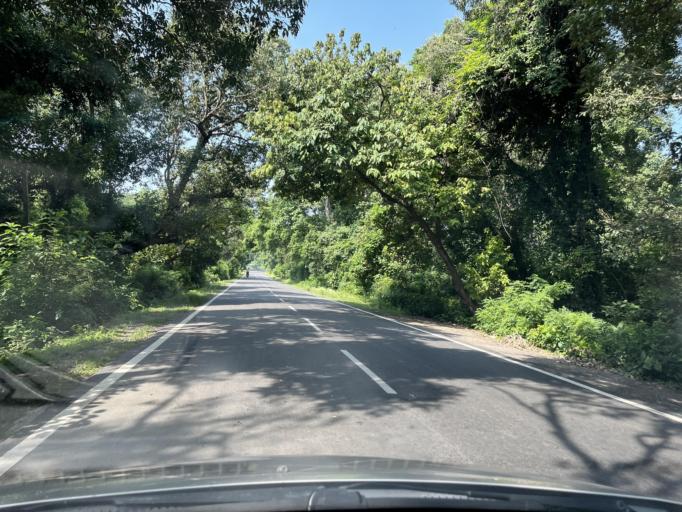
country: IN
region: Uttarakhand
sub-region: Naini Tal
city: Kaladhungi
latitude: 29.2184
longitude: 79.2305
